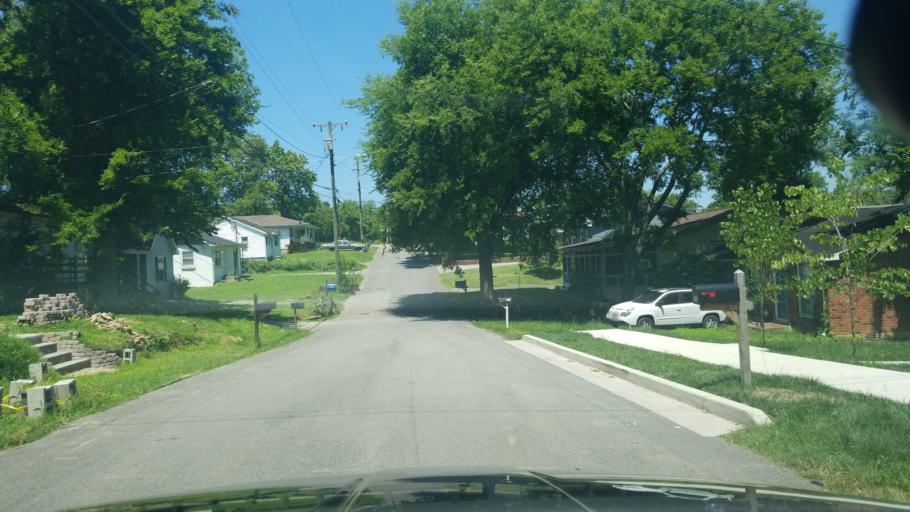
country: US
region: Tennessee
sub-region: Davidson County
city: Belle Meade
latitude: 36.1561
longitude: -86.8609
